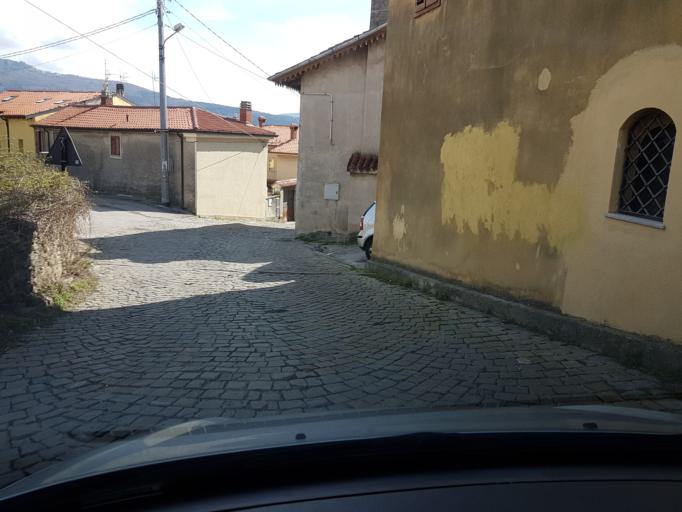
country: IT
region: Friuli Venezia Giulia
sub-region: Provincia di Trieste
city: Domio
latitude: 45.6221
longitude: 13.8366
